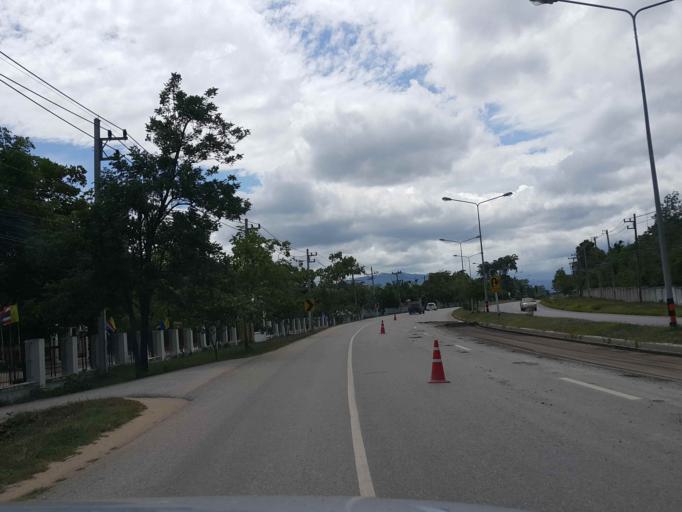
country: TH
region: Tak
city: Tak
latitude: 16.8780
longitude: 99.1455
